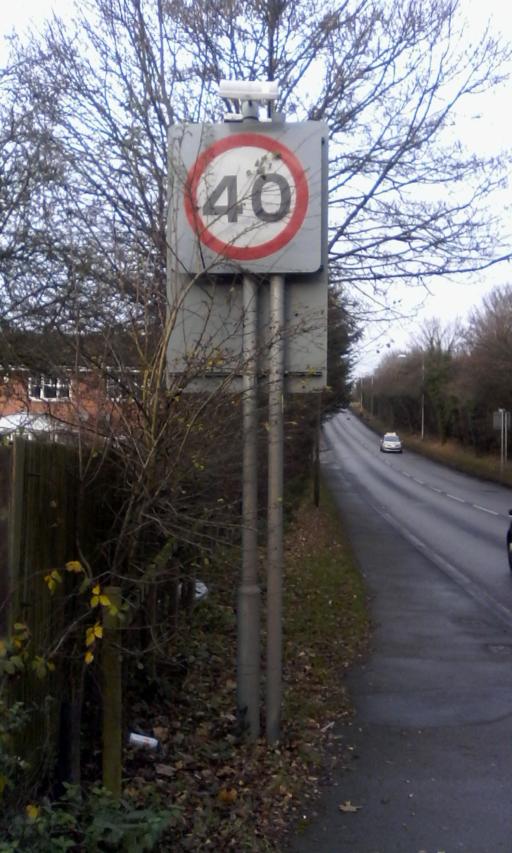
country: GB
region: England
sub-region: Nottinghamshire
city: Arnold
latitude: 52.9823
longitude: -1.0893
